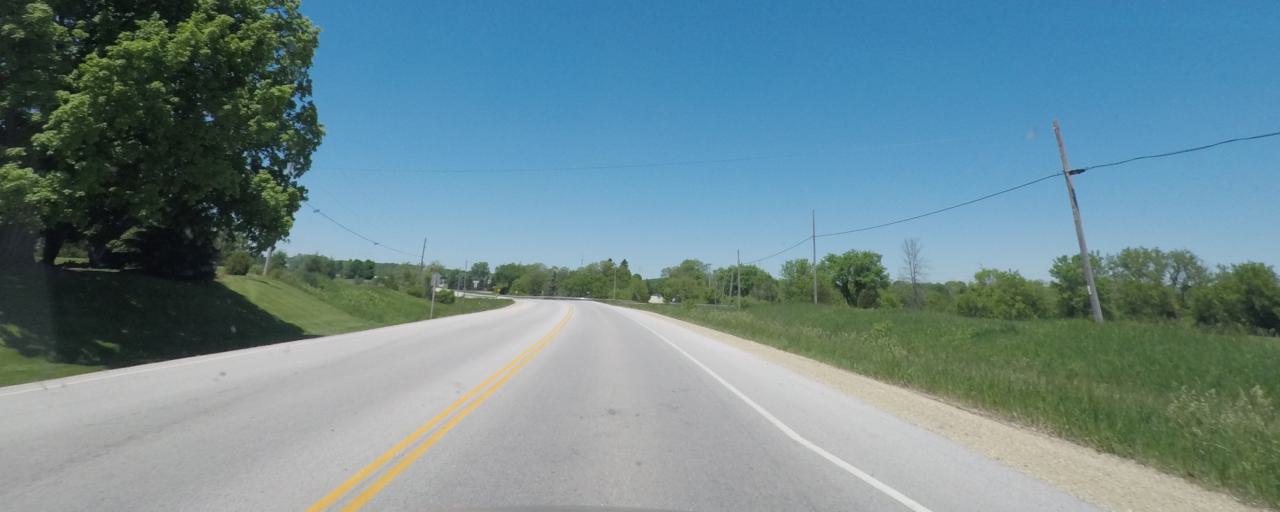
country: US
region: Wisconsin
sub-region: Washington County
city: West Bend
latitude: 43.4508
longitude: -88.1939
